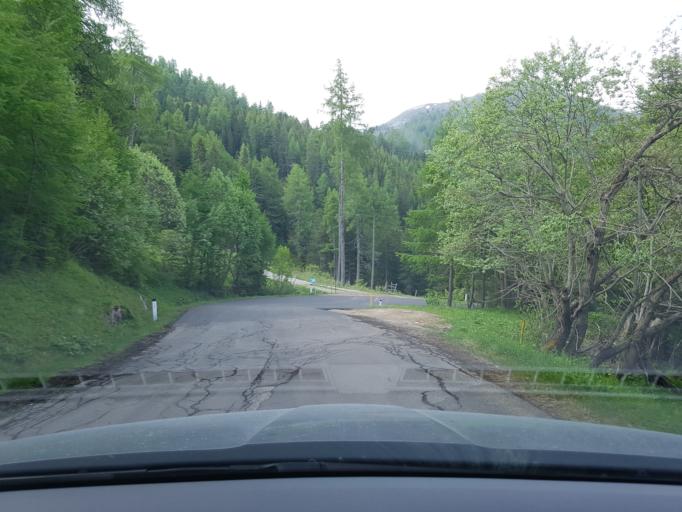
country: AT
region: Salzburg
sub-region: Politischer Bezirk Tamsweg
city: Thomatal
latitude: 46.9711
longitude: 13.7640
